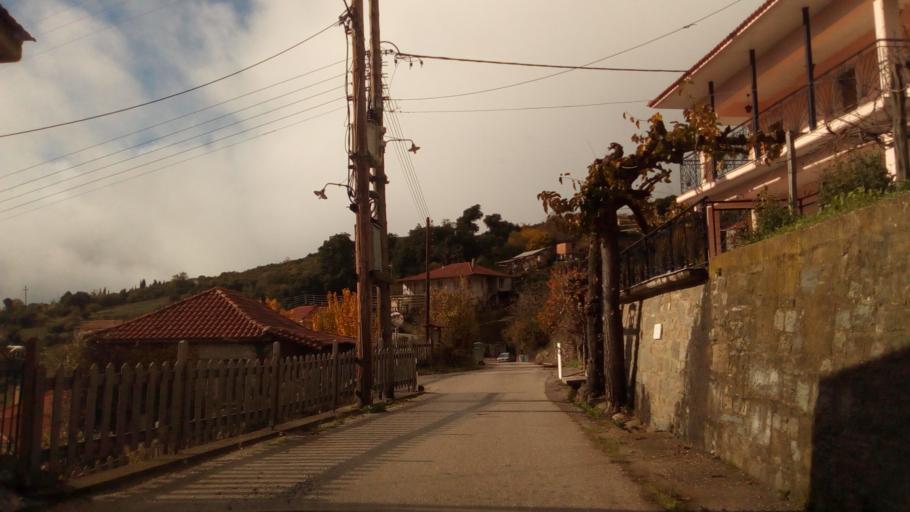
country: GR
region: West Greece
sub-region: Nomos Aitolias kai Akarnanias
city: Nafpaktos
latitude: 38.5422
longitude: 21.9301
